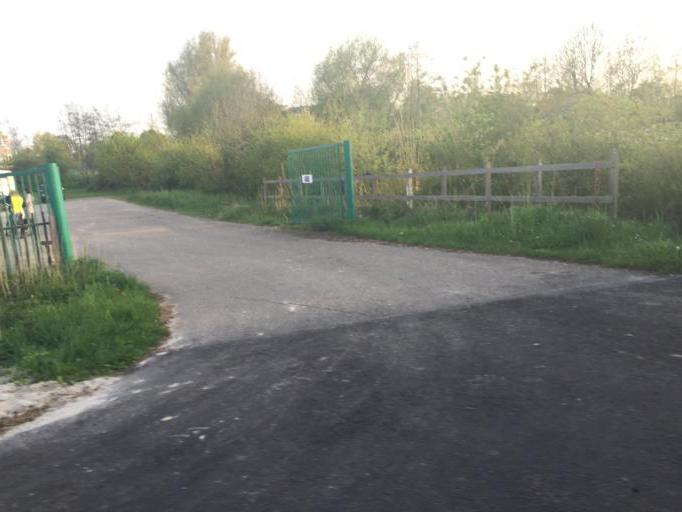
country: NL
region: Utrecht
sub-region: Gemeente Woerden
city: Woerden
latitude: 52.0949
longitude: 4.8987
